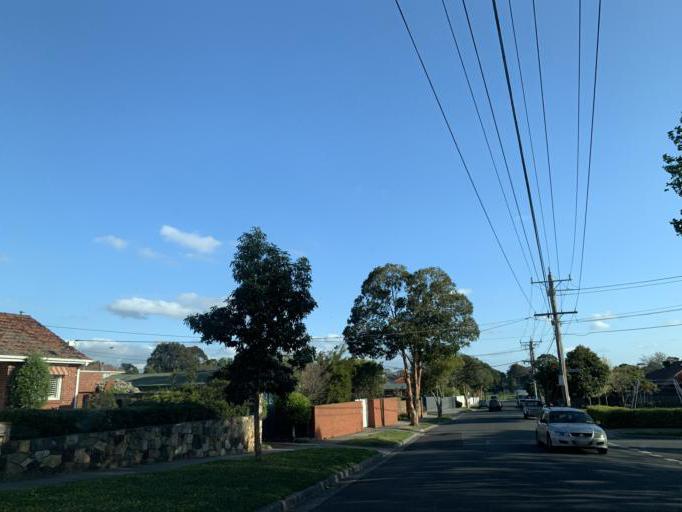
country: AU
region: Victoria
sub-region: Kingston
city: Mordialloc
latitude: -37.9886
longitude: 145.0889
